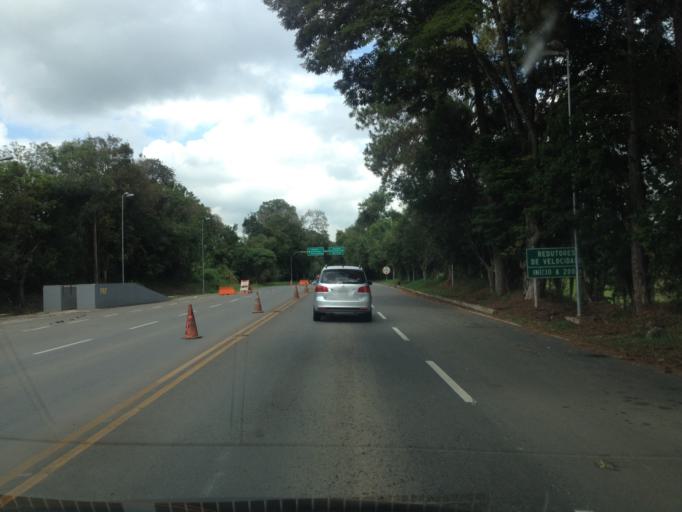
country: BR
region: Minas Gerais
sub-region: Itanhandu
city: Itanhandu
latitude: -22.2450
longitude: -44.9353
